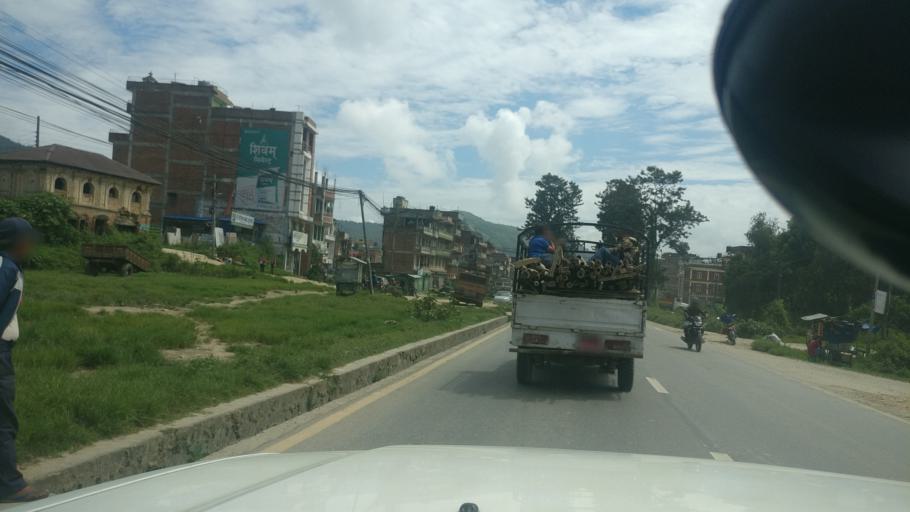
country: NP
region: Central Region
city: Banepa
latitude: 27.6325
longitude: 85.5106
